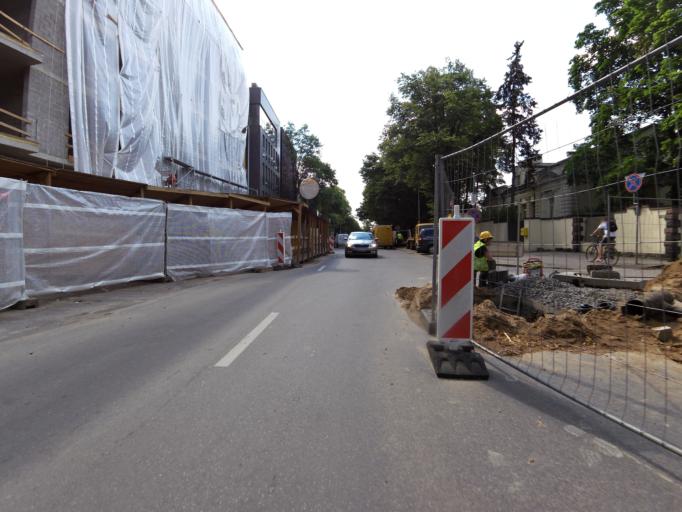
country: LT
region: Vilnius County
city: Naujamiestis
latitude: 54.6825
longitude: 25.2708
